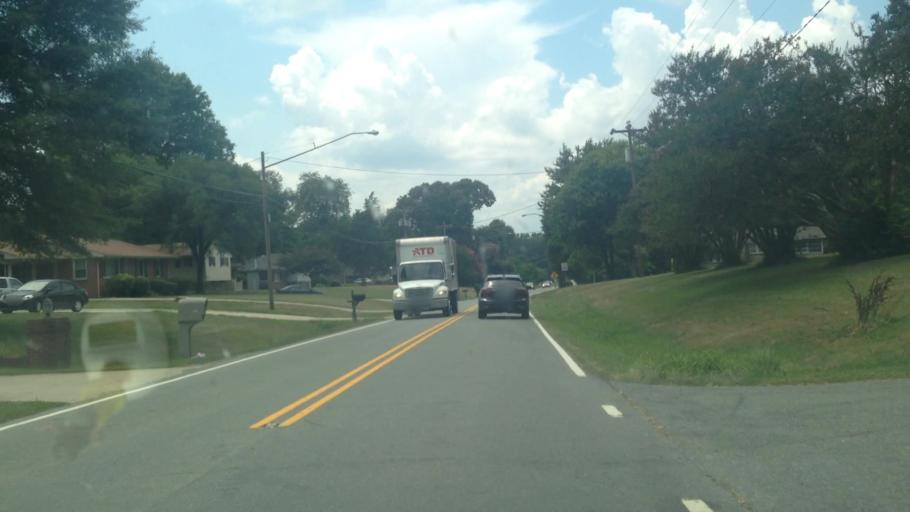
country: US
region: North Carolina
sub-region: Forsyth County
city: Rural Hall
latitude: 36.1950
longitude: -80.2573
